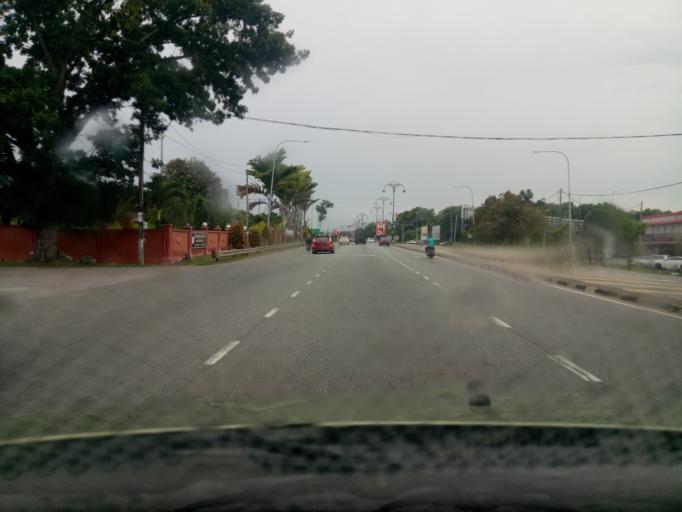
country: MY
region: Kedah
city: Sungai Petani
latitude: 5.6785
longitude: 100.5083
